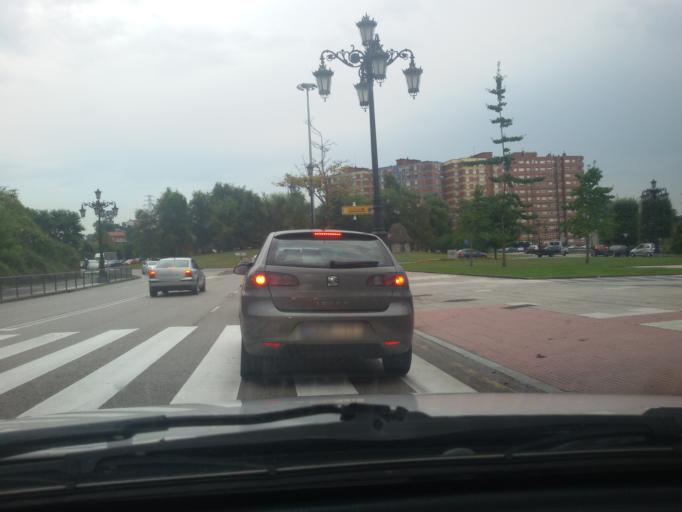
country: ES
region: Asturias
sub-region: Province of Asturias
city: Oviedo
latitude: 43.3723
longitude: -5.8470
